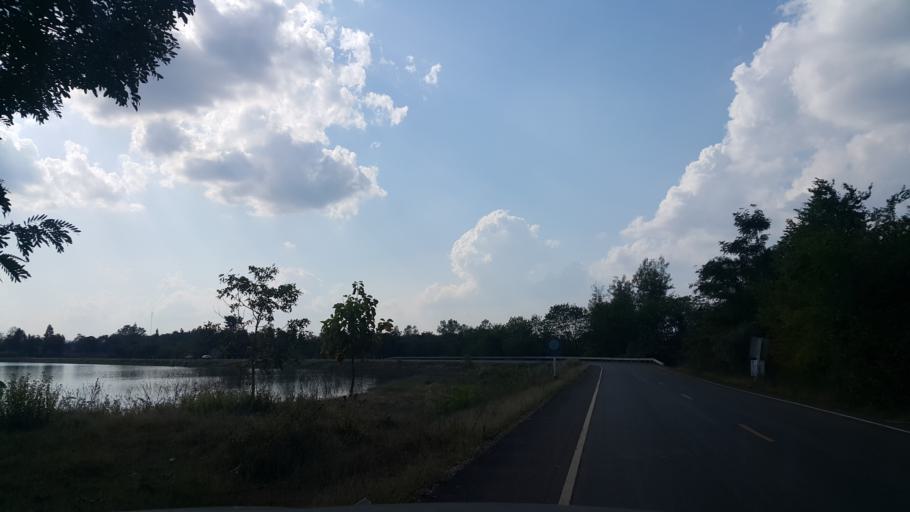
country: TH
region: Lamphun
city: Ban Thi
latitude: 18.5470
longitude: 99.1083
